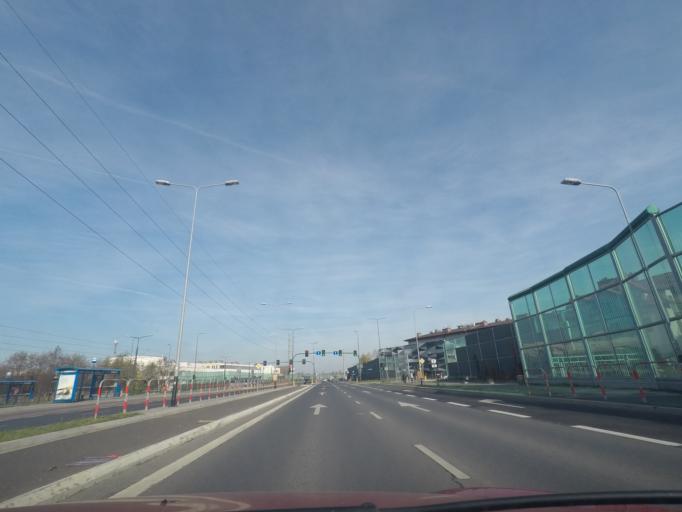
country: PL
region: Lesser Poland Voivodeship
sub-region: Krakow
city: Sidzina
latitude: 50.0236
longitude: 19.9016
